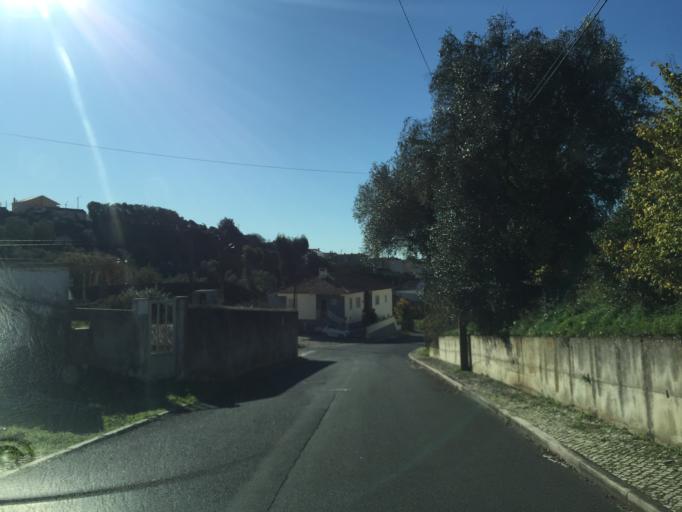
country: PT
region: Lisbon
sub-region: Sintra
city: Pero Pinheiro
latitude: 38.8485
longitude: -9.3173
